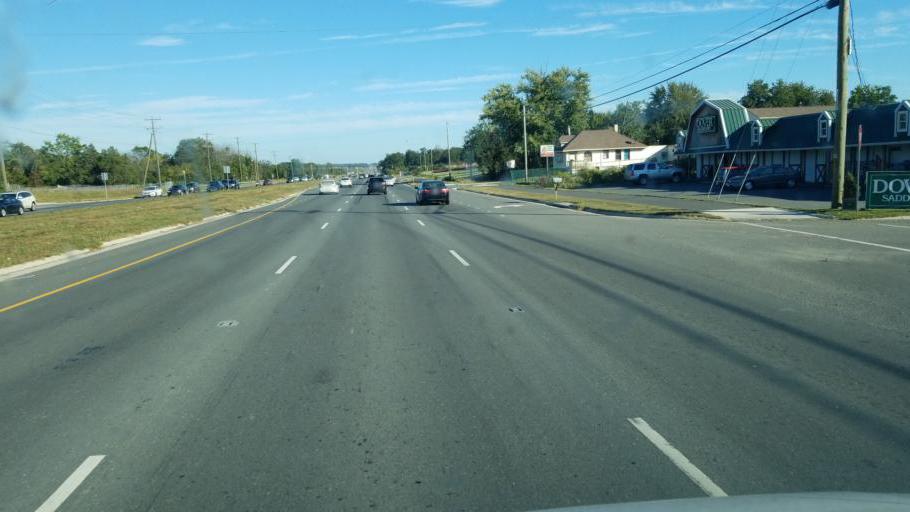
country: US
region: Virginia
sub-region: Loudoun County
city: South Riding
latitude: 38.9181
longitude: -77.4907
